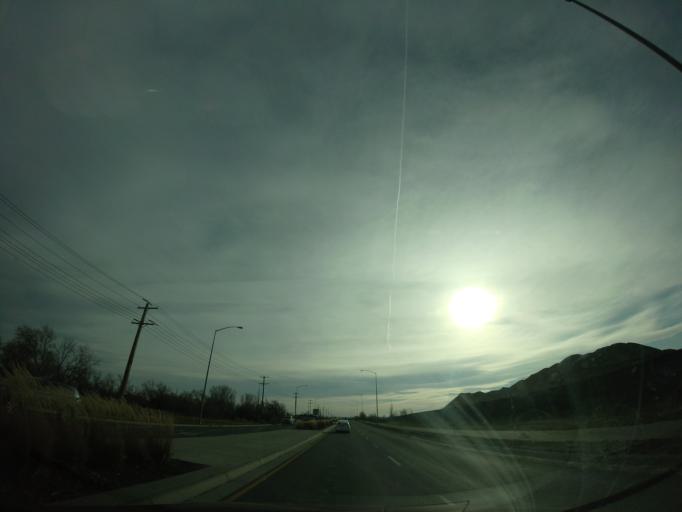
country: US
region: Montana
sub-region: Yellowstone County
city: Billings
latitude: 45.7451
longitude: -108.6175
